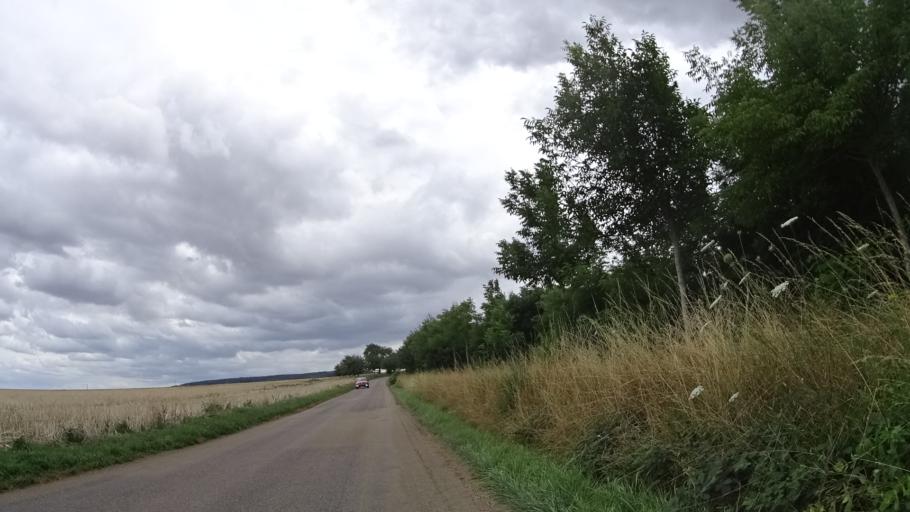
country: FR
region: Bourgogne
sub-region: Departement de l'Yonne
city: Cezy
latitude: 47.9660
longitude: 3.3570
